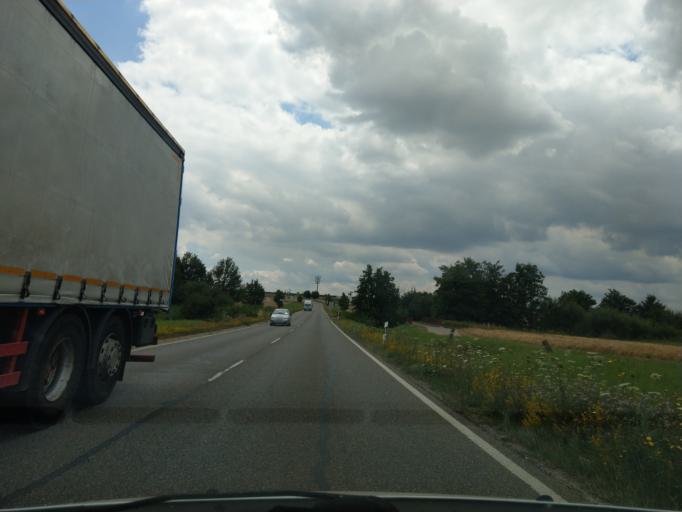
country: DE
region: Baden-Wuerttemberg
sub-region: Regierungsbezirk Stuttgart
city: Ostfildern
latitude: 48.7027
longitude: 9.2477
